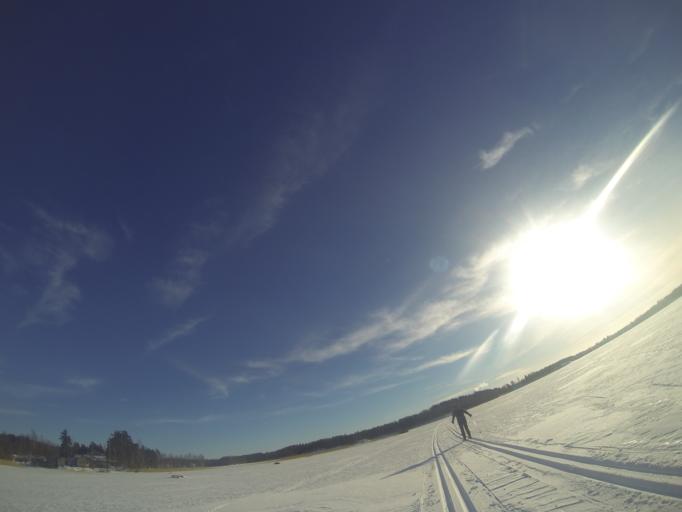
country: FI
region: Southern Savonia
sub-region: Savonlinna
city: Savonlinna
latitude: 61.8844
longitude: 28.9057
